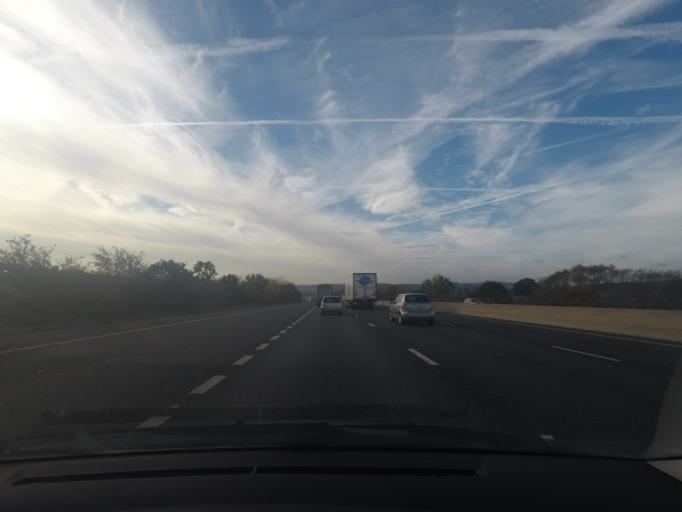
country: GB
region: England
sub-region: City and Borough of Wakefield
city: Crigglestone
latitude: 53.6168
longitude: -1.5513
